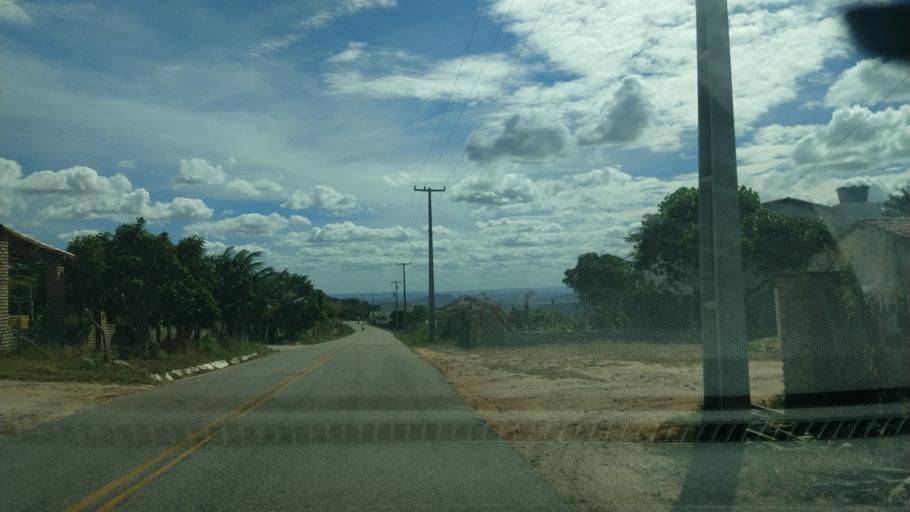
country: BR
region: Rio Grande do Norte
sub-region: Sao Jose Do Campestre
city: Sao Jose do Campestre
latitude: -6.4205
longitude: -35.7546
